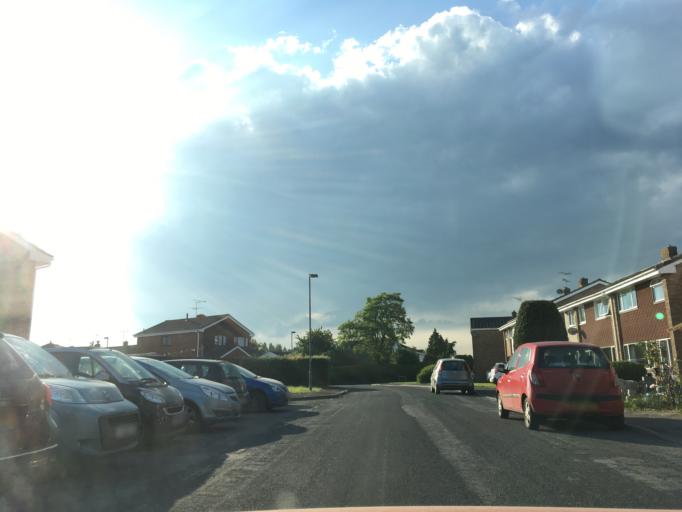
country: GB
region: England
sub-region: South Gloucestershire
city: Charfield
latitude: 51.6263
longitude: -2.4015
